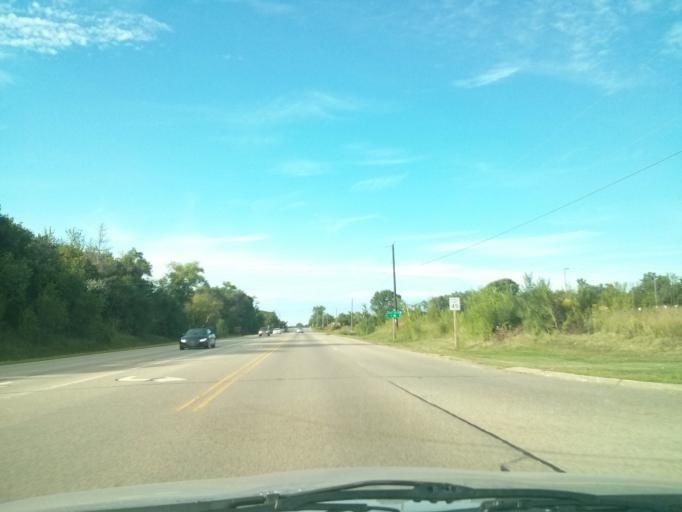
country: US
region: Minnesota
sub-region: Washington County
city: Lakeland
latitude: 44.9390
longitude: -92.7315
